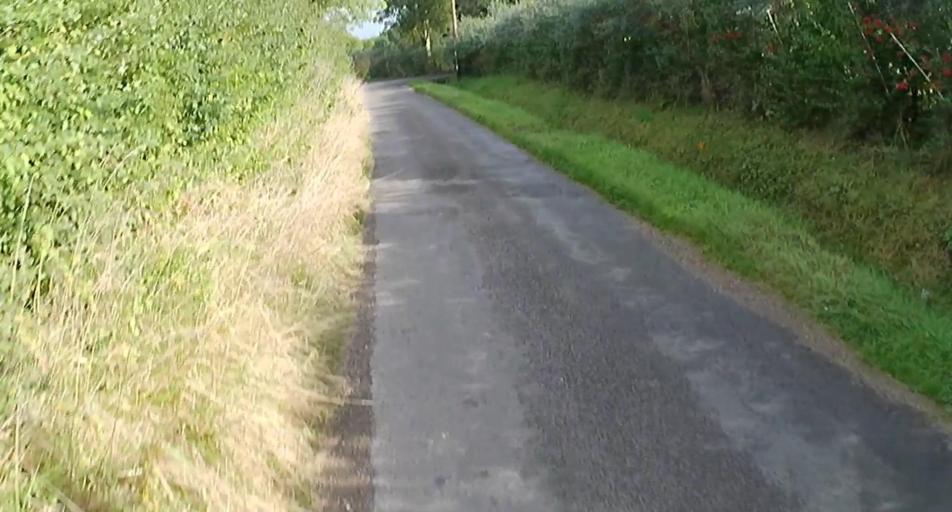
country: GB
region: England
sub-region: Hampshire
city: Tadley
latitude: 51.3116
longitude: -1.1609
